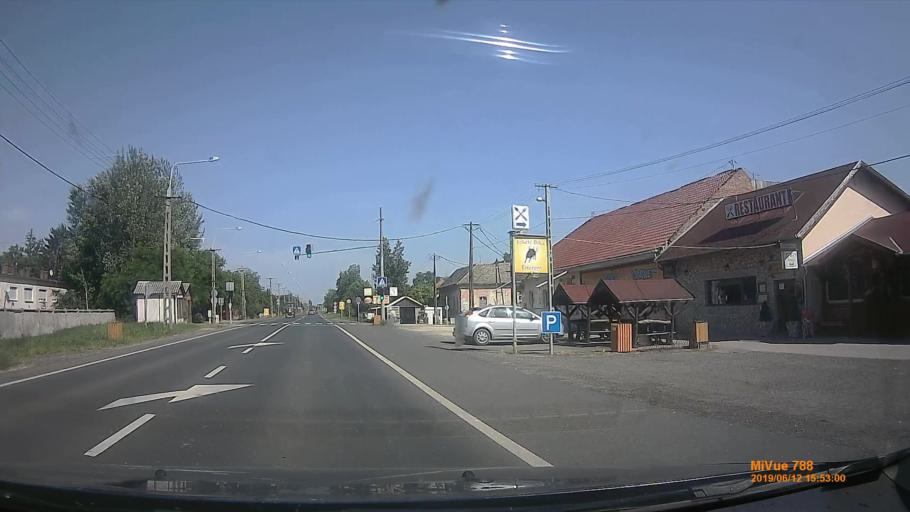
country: HU
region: Csongrad
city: Apatfalva
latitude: 46.1745
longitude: 20.5789
